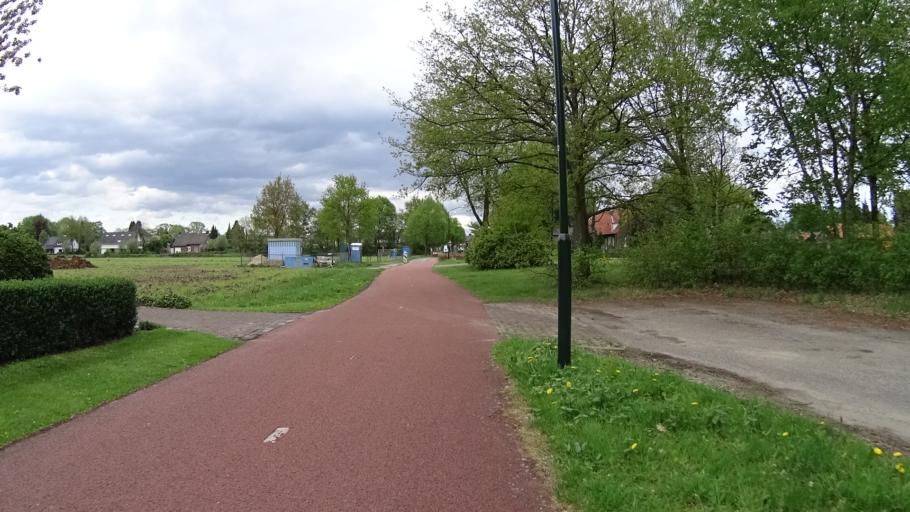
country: NL
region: North Brabant
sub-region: Gemeente Nuenen, Gerwen en Nederwetten
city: Nuenen
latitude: 51.4847
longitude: 5.5608
